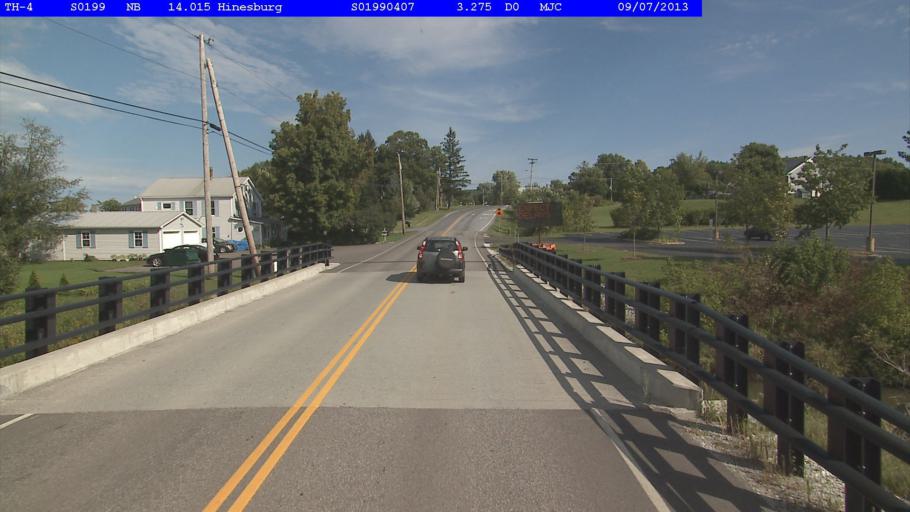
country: US
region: Vermont
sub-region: Chittenden County
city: Hinesburg
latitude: 44.3251
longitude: -73.1101
